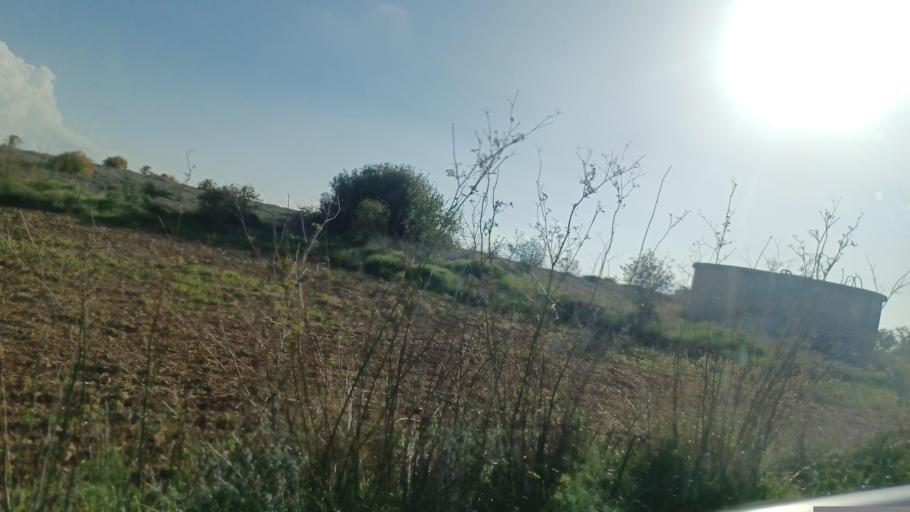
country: CY
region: Pafos
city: Mesogi
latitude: 34.8062
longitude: 32.4901
